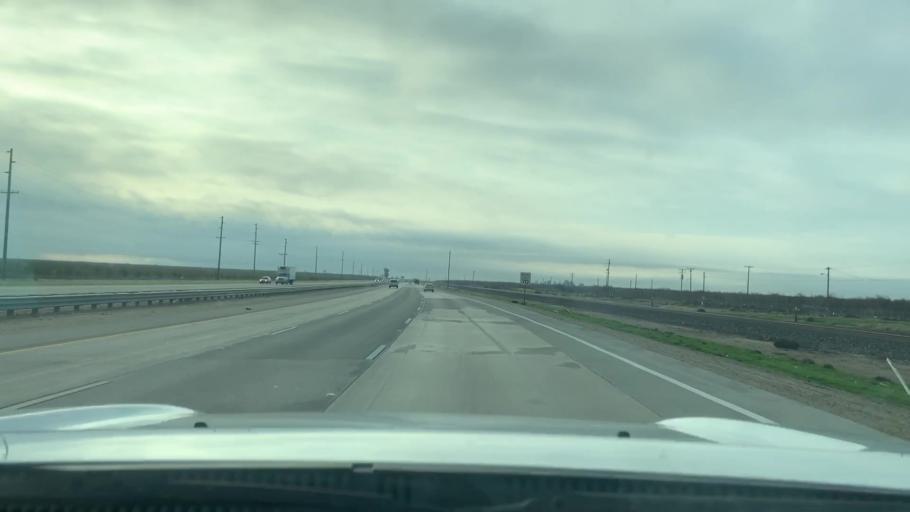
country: US
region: California
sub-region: Kern County
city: Shafter
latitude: 35.5533
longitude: -119.1971
